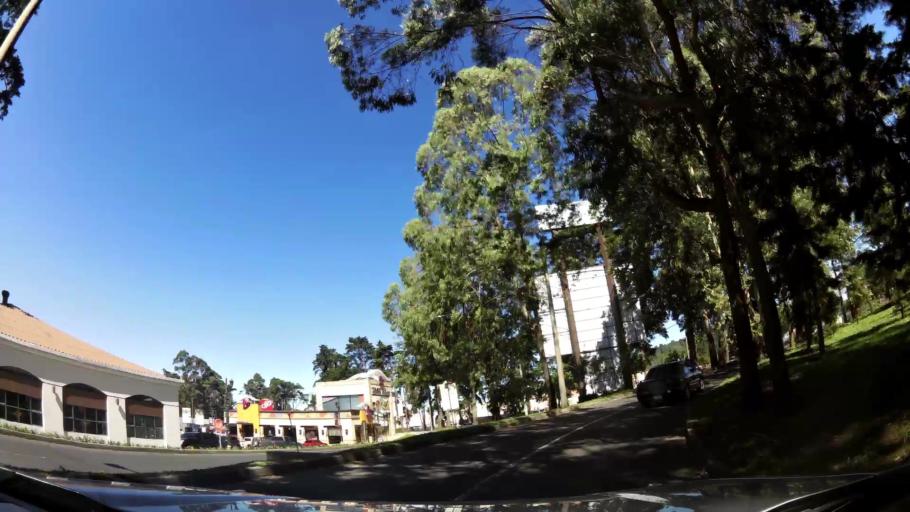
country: GT
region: Guatemala
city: Santa Catarina Pinula
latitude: 14.5543
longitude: -90.4559
